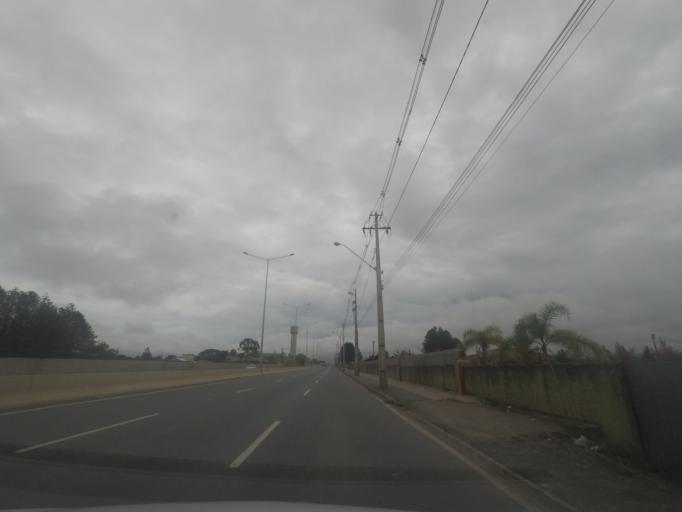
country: BR
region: Parana
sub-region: Piraquara
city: Piraquara
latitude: -25.4510
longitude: -49.1225
